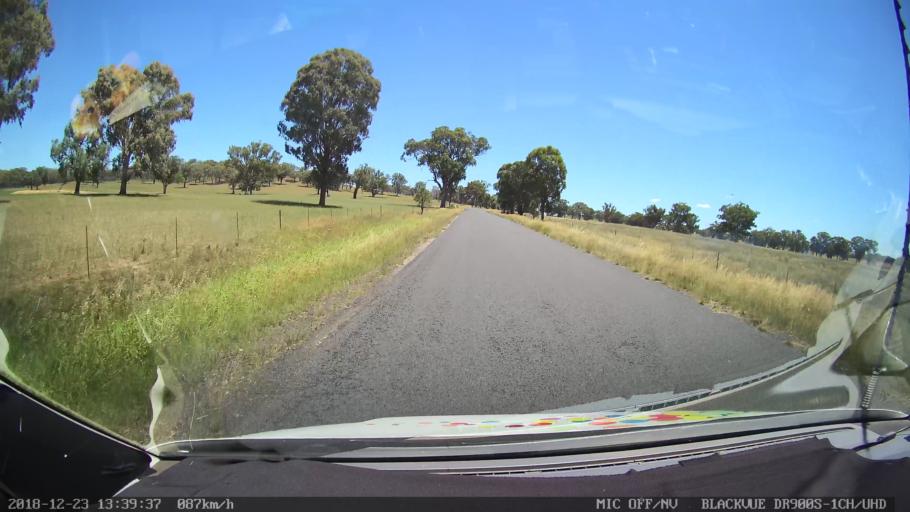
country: AU
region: New South Wales
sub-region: Armidale Dumaresq
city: Armidale
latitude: -30.4597
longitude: 151.1996
